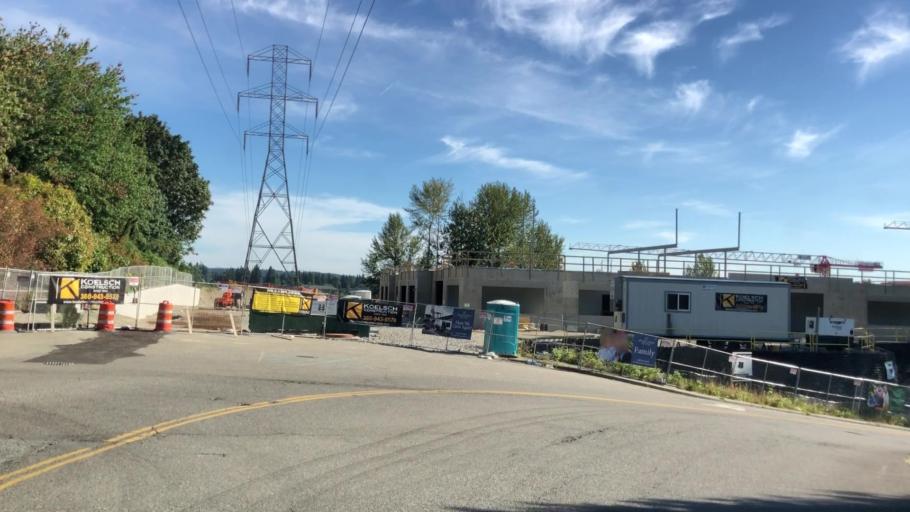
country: US
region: Washington
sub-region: King County
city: Kingsgate
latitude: 47.7143
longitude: -122.1756
